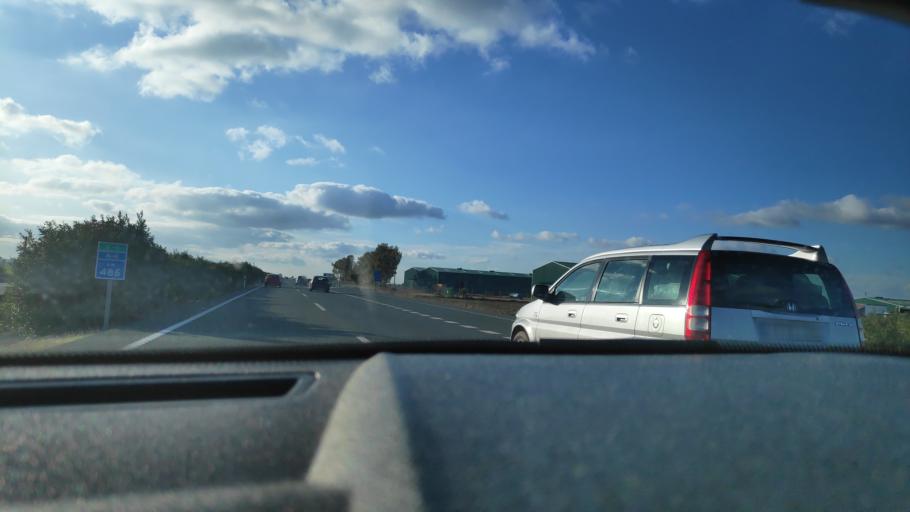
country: ES
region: Andalusia
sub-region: Provincia de Sevilla
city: La Campana
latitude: 37.5084
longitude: -5.4225
